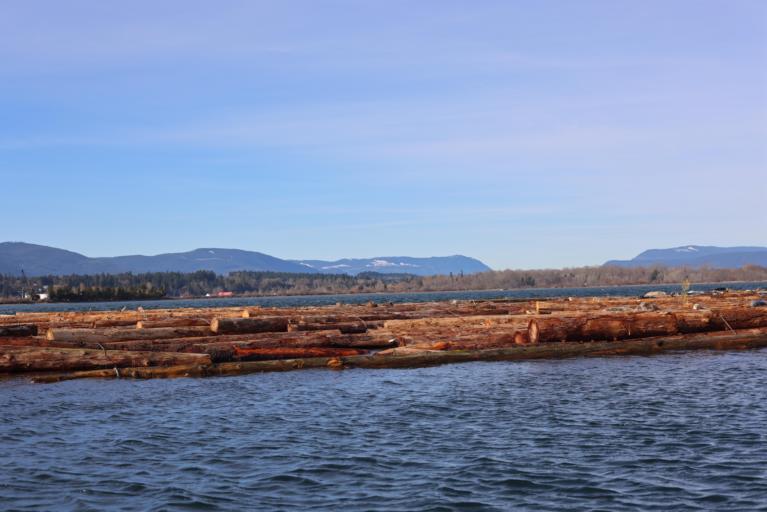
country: CA
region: British Columbia
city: Duncan
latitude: 48.7536
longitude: -123.6215
